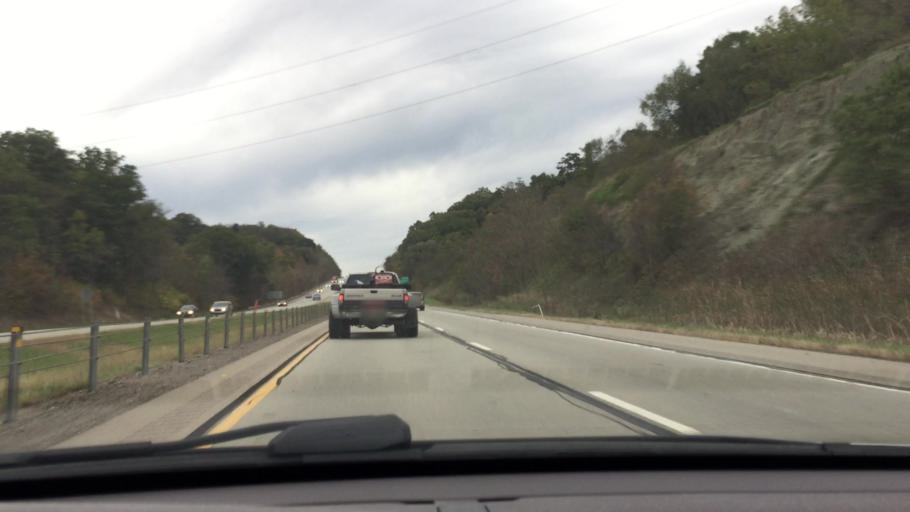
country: US
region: Pennsylvania
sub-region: Beaver County
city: Ambridge
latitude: 40.5800
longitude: -80.2901
